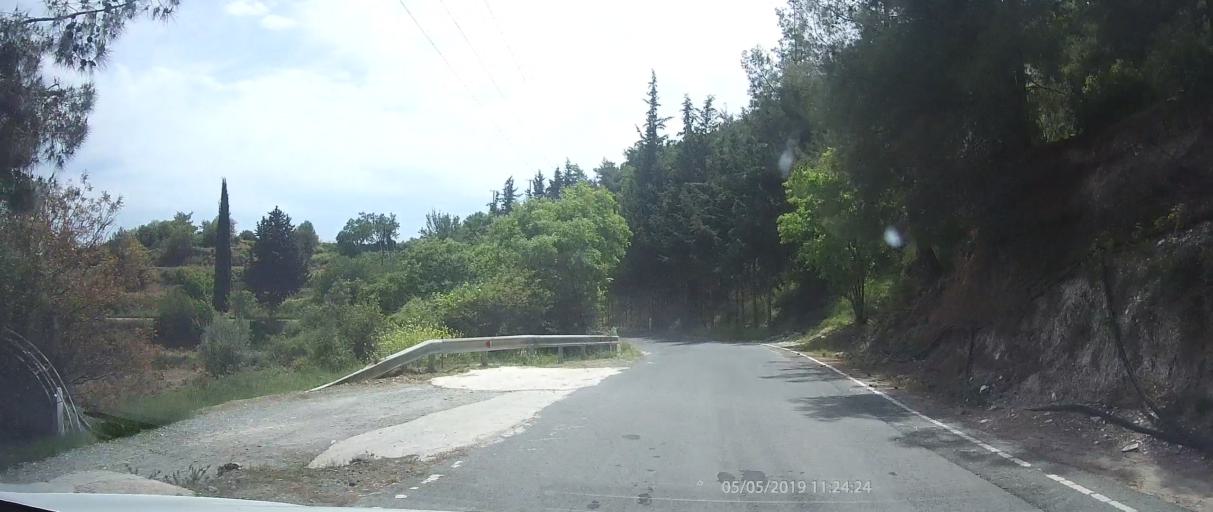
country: CY
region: Limassol
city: Pachna
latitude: 34.9218
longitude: 32.6394
